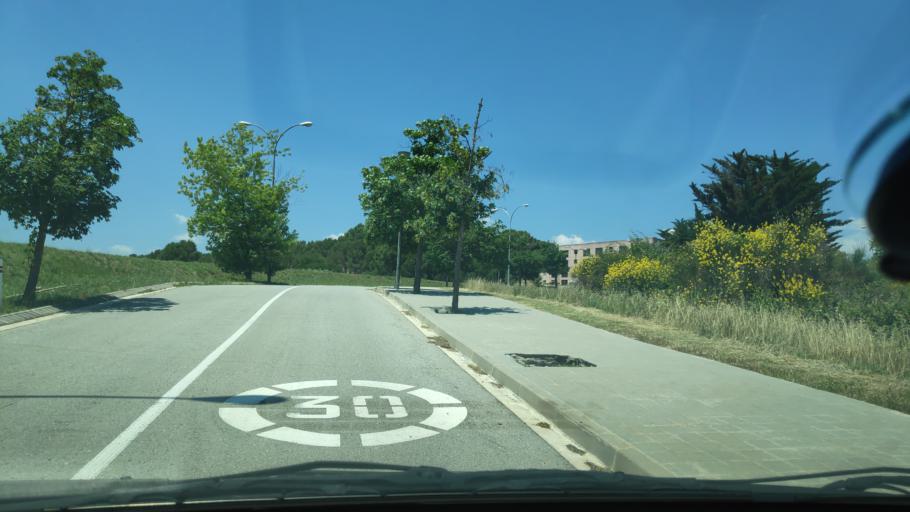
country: ES
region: Catalonia
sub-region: Provincia de Barcelona
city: Barbera del Valles
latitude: 41.4975
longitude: 2.1013
